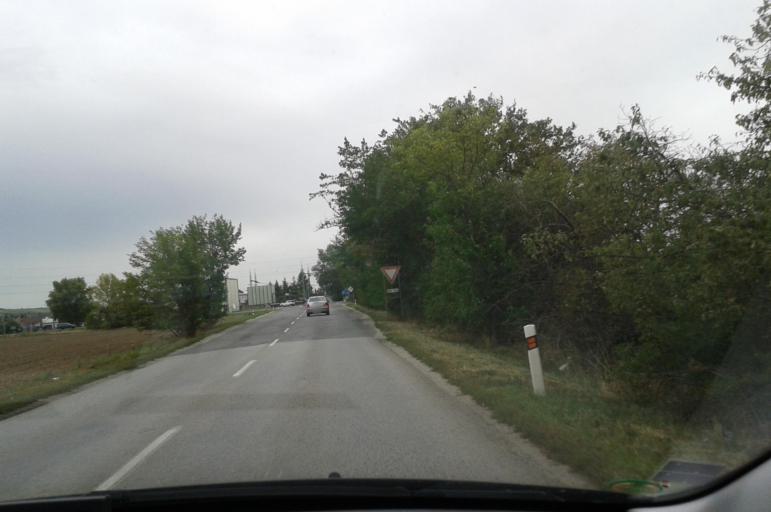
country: SK
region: Trnavsky
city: Leopoldov
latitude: 48.4374
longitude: 17.7676
